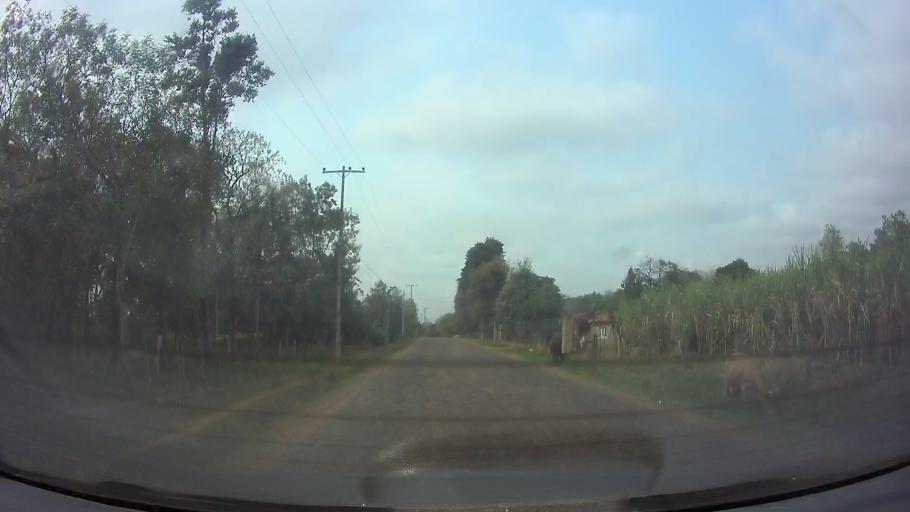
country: PY
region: Cordillera
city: Arroyos y Esteros
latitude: -25.0436
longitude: -57.1004
